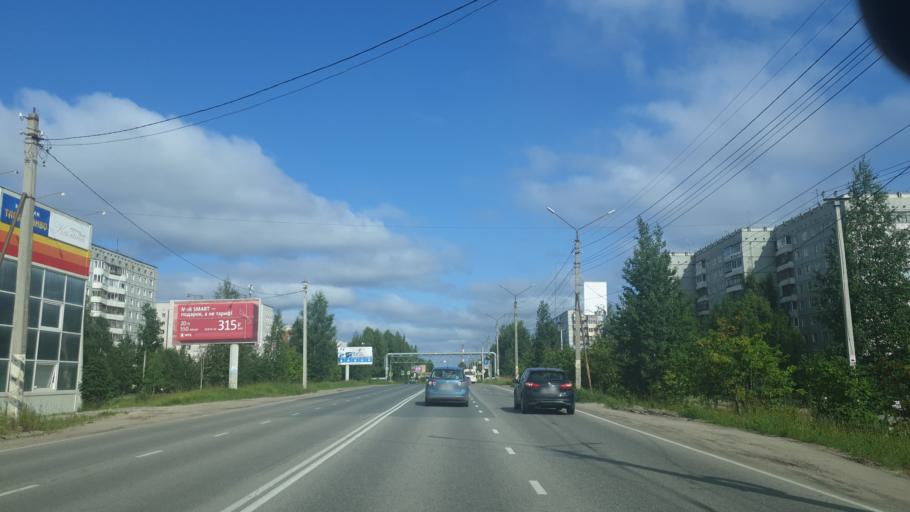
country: RU
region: Komi Republic
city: Ezhva
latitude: 61.7852
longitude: 50.7454
